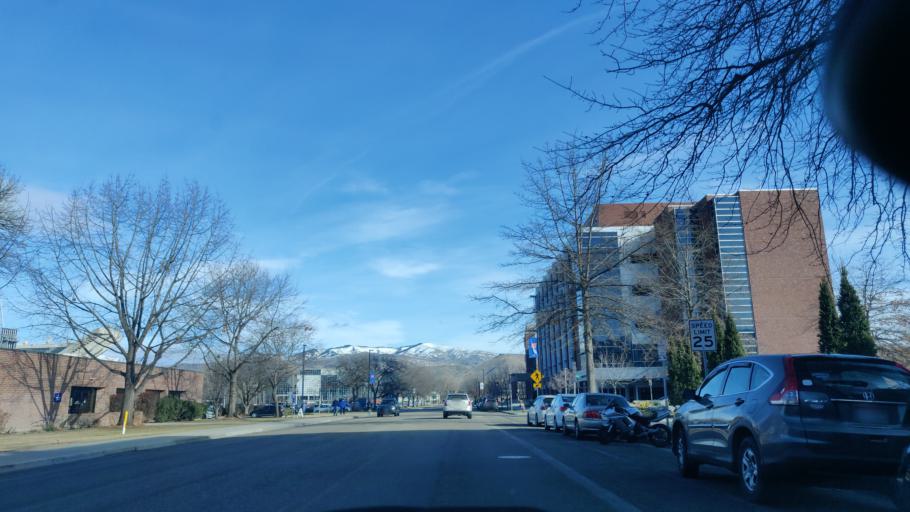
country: US
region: Idaho
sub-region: Ada County
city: Boise
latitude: 43.6010
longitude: -116.1982
